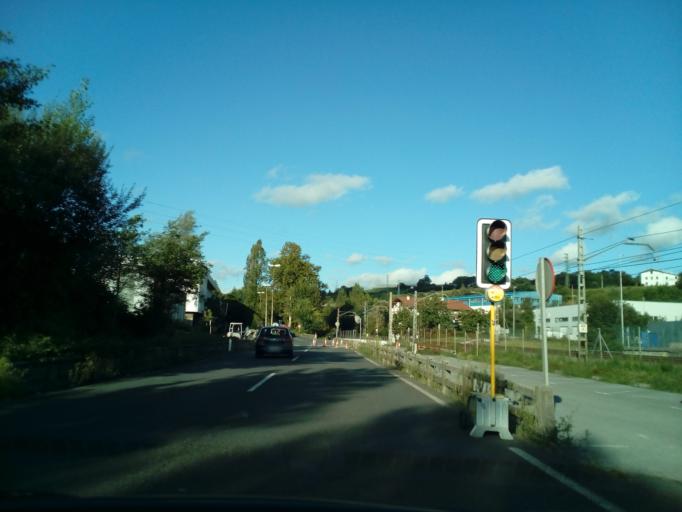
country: ES
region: Basque Country
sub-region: Provincia de Guipuzcoa
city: Andoain
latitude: 43.2267
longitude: -2.0077
